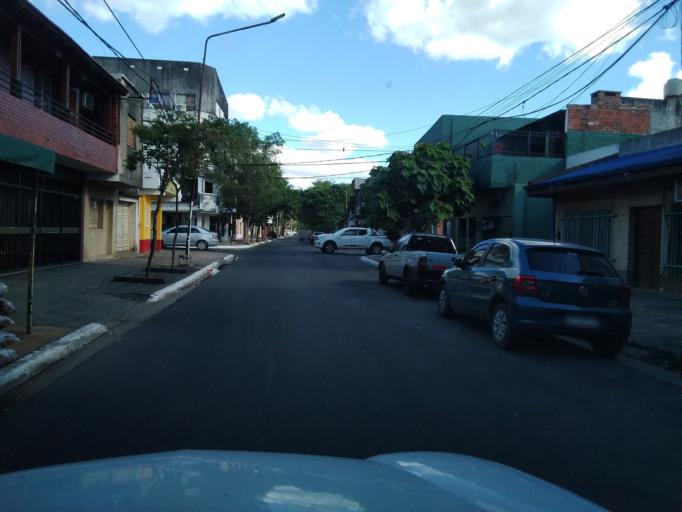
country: AR
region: Corrientes
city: Corrientes
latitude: -27.4773
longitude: -58.8315
